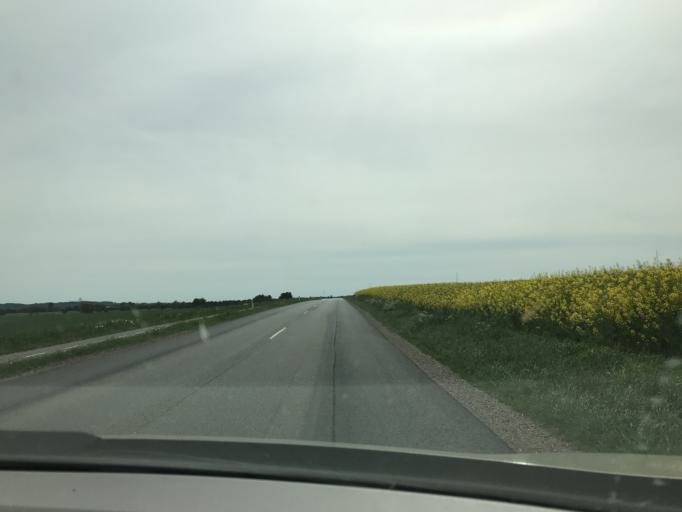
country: DK
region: Central Jutland
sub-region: Norddjurs Kommune
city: Allingabro
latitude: 56.4891
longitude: 10.3247
